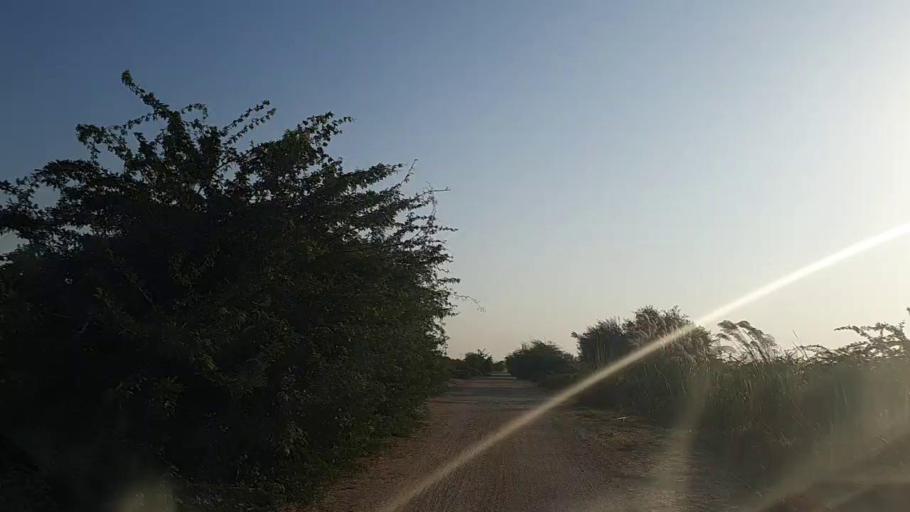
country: PK
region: Sindh
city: Jati
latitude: 24.4211
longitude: 68.1861
